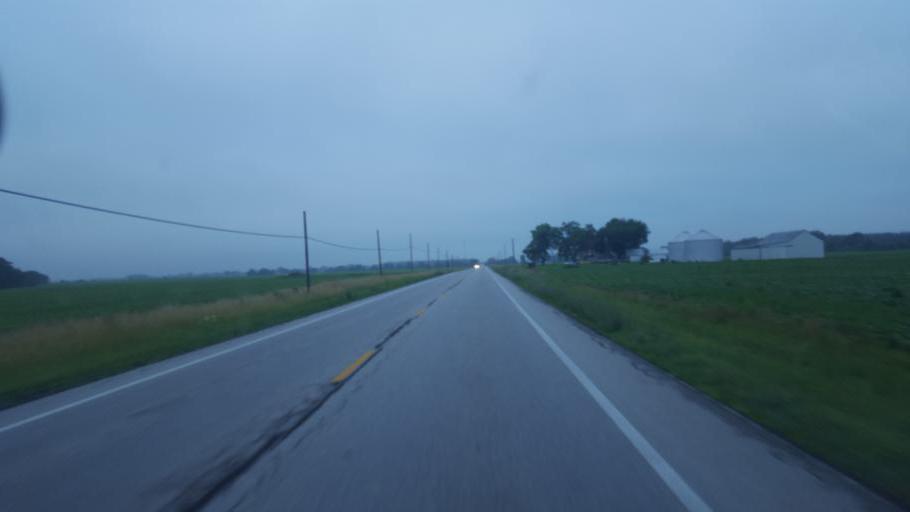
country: US
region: Ohio
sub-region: Madison County
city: Mount Sterling
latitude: 39.7048
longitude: -83.2790
